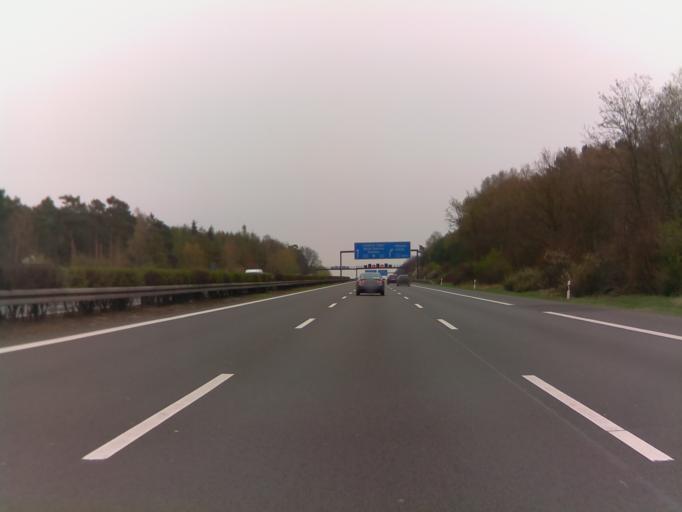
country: DE
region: Brandenburg
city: Fichtenwalde
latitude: 52.3008
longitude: 12.8951
